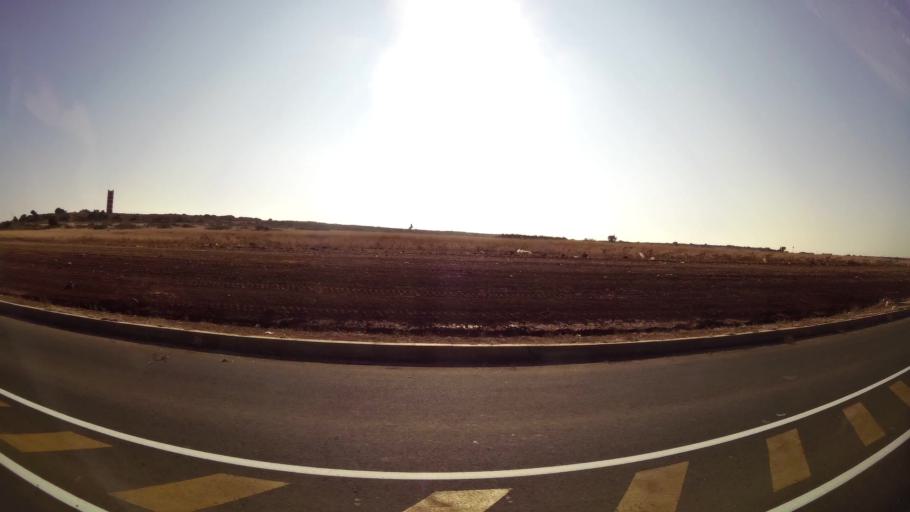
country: ZA
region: Orange Free State
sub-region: Mangaung Metropolitan Municipality
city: Bloemfontein
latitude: -29.1850
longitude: 26.2020
